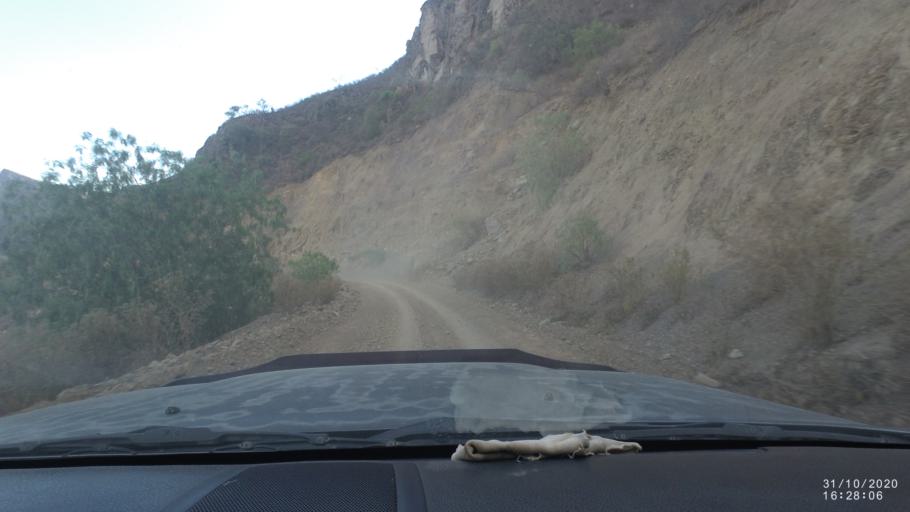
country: BO
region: Chuquisaca
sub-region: Provincia Zudanez
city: Mojocoya
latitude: -18.4104
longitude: -64.5864
